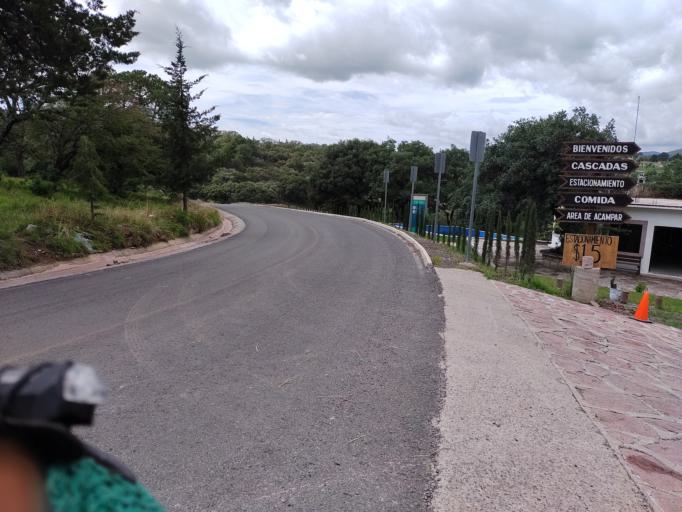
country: MX
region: Mexico
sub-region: Aculco
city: Gunyo Poniente (San Jose Gunyo)
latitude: 20.1125
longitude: -99.8803
